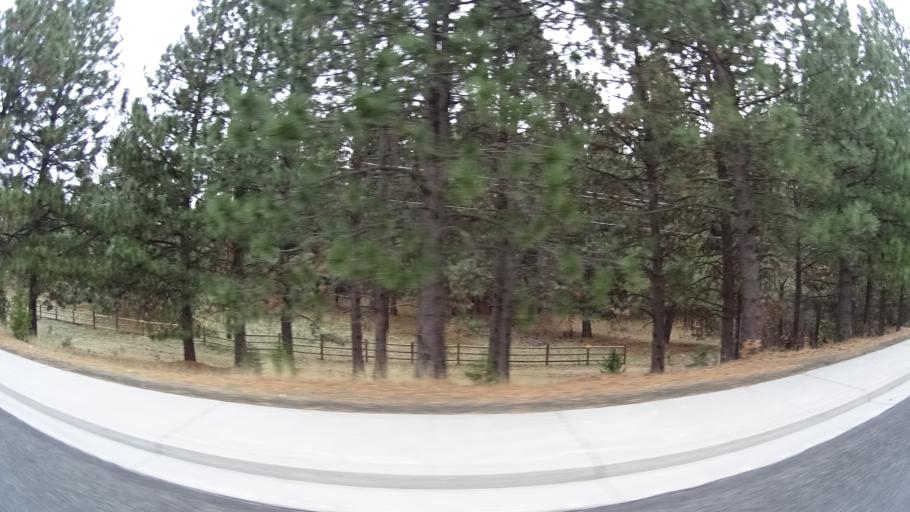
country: US
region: California
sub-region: Siskiyou County
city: Weed
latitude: 41.4088
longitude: -122.3790
